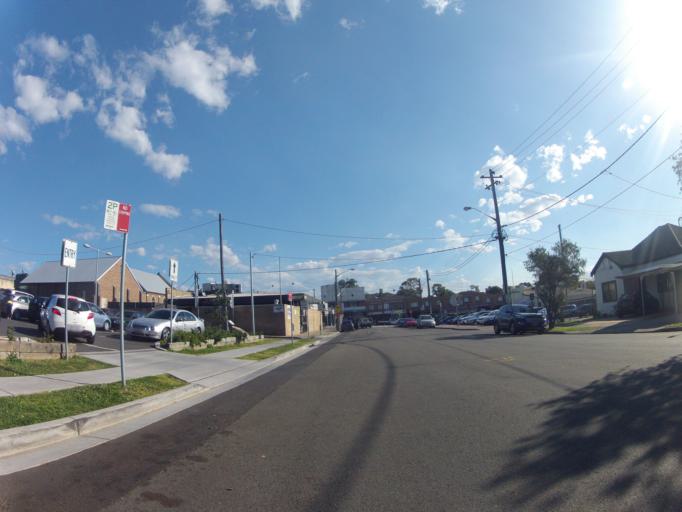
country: AU
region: New South Wales
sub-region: Hurstville
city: Penshurst
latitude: -33.9700
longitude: 151.0806
